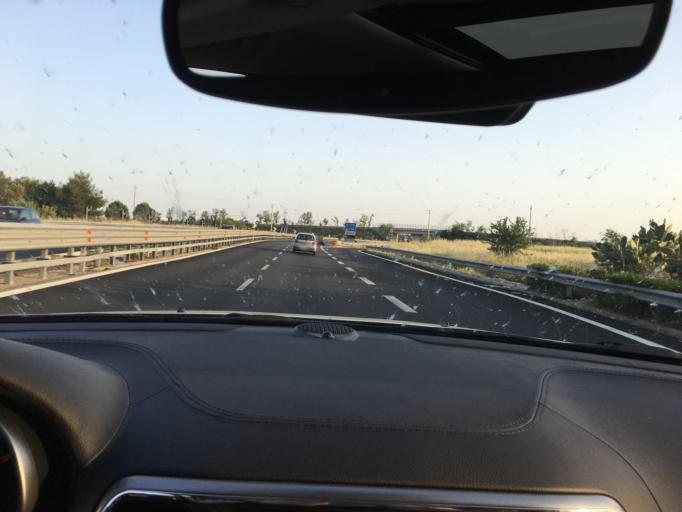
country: IT
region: Apulia
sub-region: Provincia di Lecce
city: Lequile
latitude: 40.2921
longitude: 18.1329
